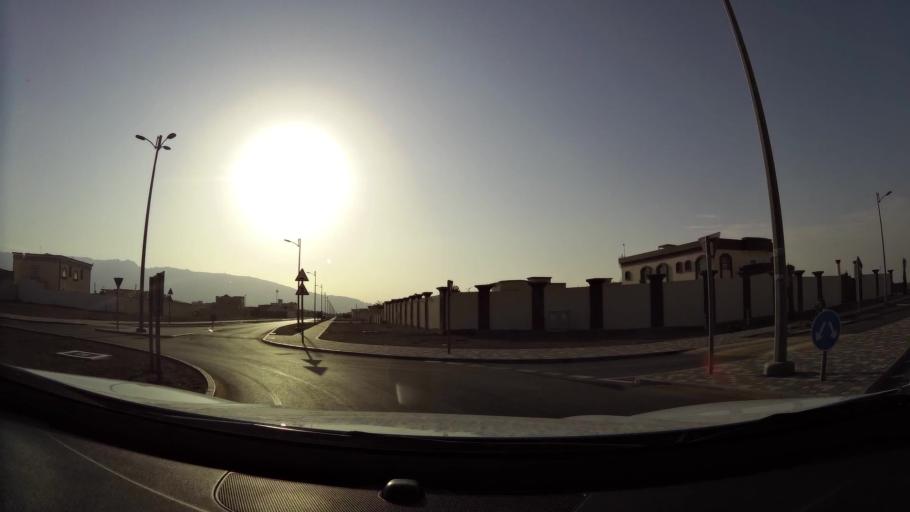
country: AE
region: Abu Dhabi
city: Al Ain
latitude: 24.1105
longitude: 55.8457
